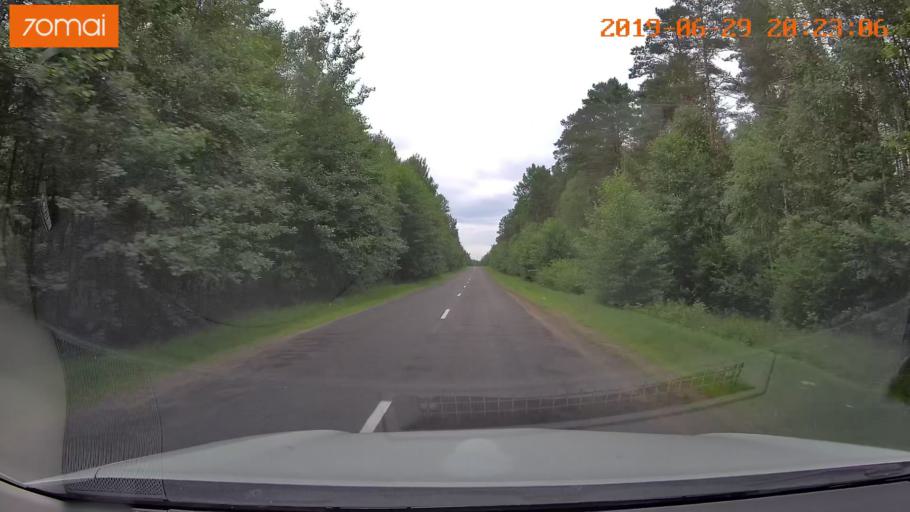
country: BY
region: Brest
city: Asnyezhytsy
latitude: 52.4401
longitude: 26.2585
